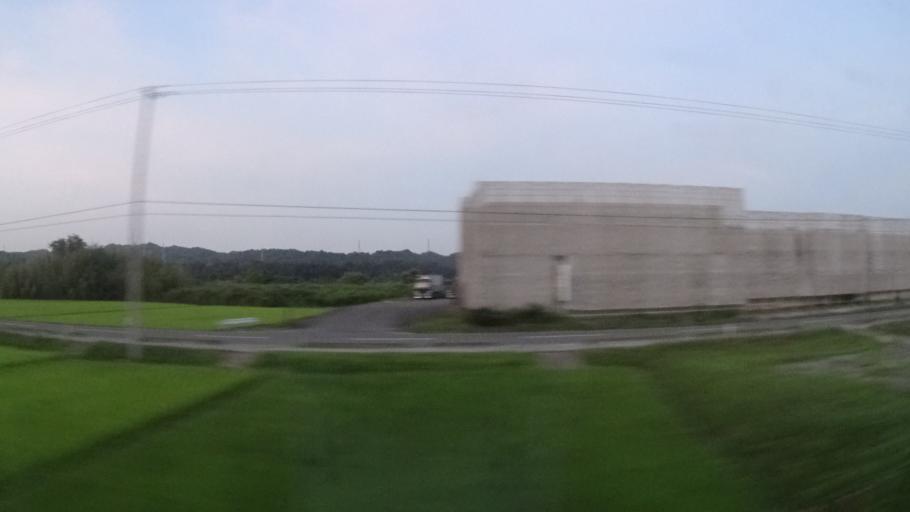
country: JP
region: Fukushima
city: Iwaki
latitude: 37.1087
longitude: 140.8624
